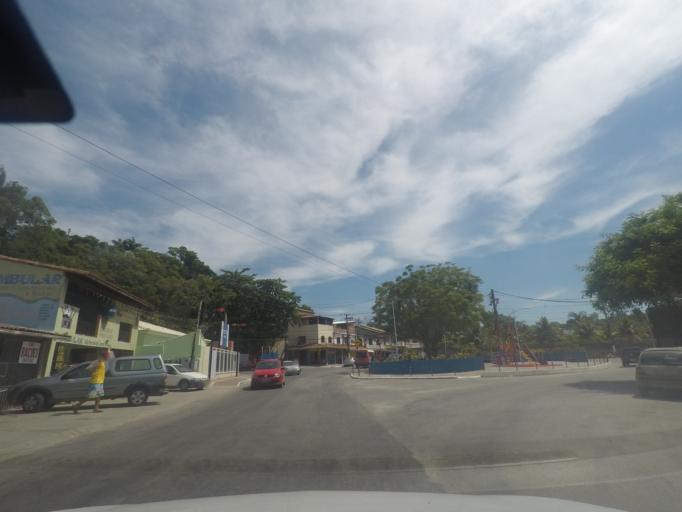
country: BR
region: Rio de Janeiro
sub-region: Marica
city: Marica
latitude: -22.9442
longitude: -42.7517
